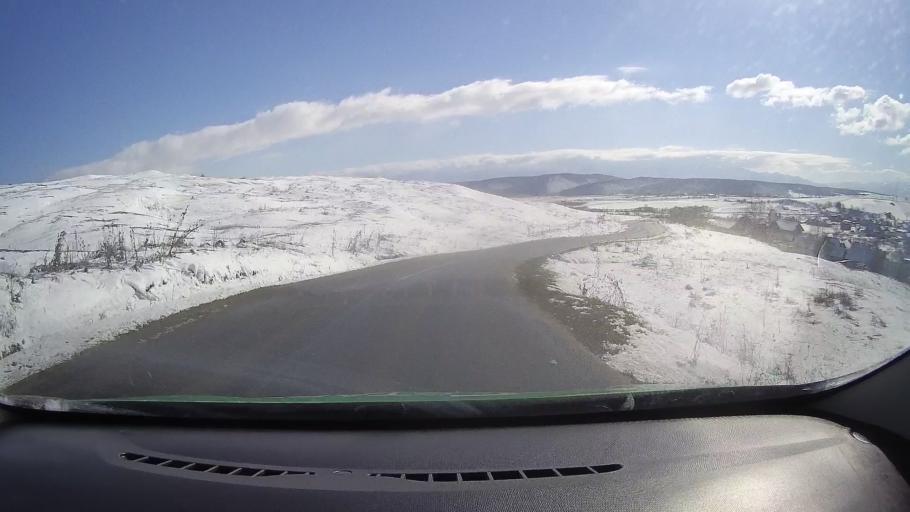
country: RO
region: Sibiu
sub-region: Comuna Rosia
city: Rosia
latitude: 45.8047
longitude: 24.2911
